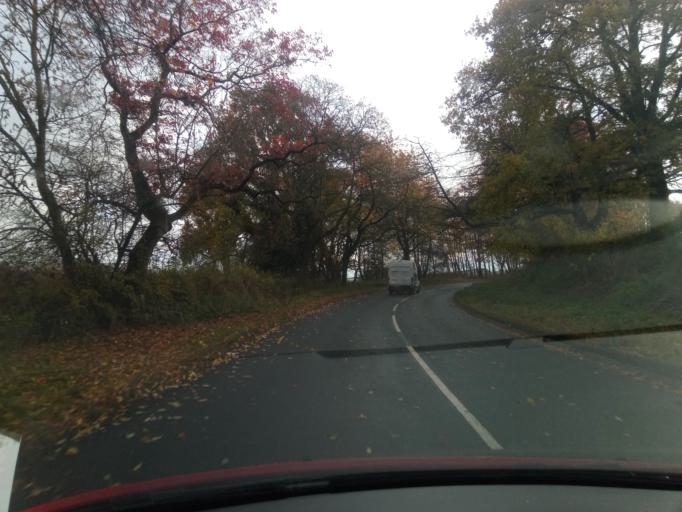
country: GB
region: England
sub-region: Northumberland
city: Birtley
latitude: 55.0681
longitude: -2.1933
